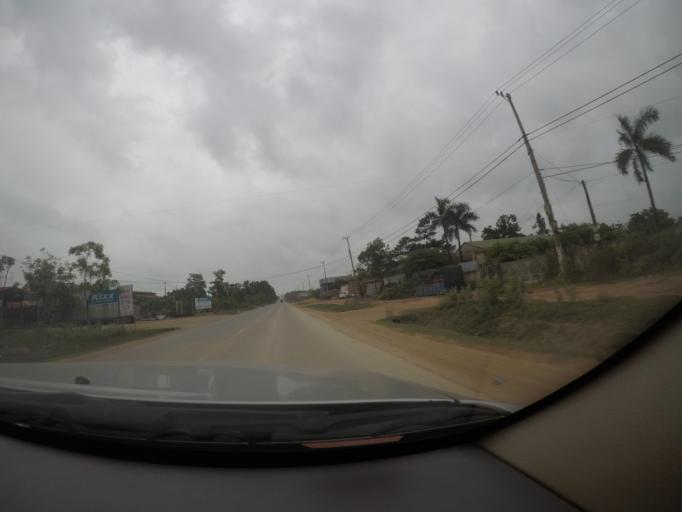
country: VN
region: Quang Tri
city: Dong Ha
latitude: 16.7902
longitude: 107.0854
